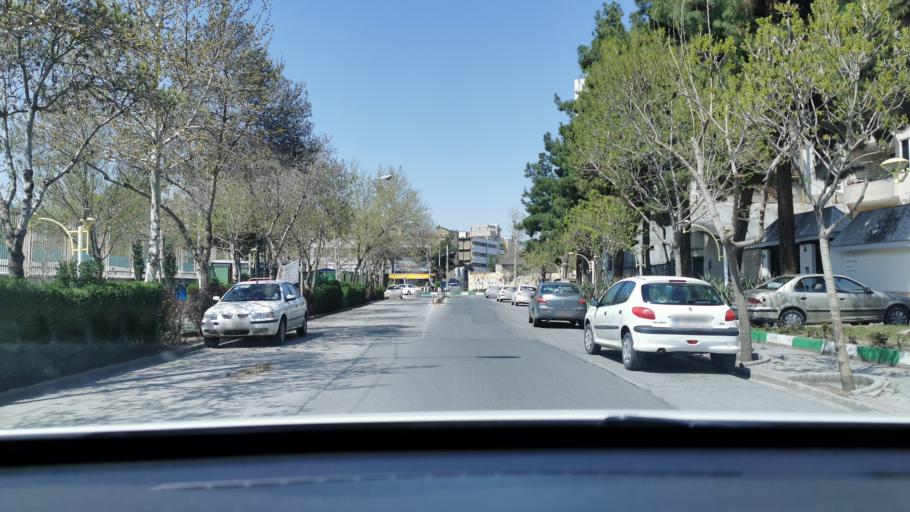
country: IR
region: Razavi Khorasan
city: Mashhad
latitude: 36.2885
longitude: 59.5812
